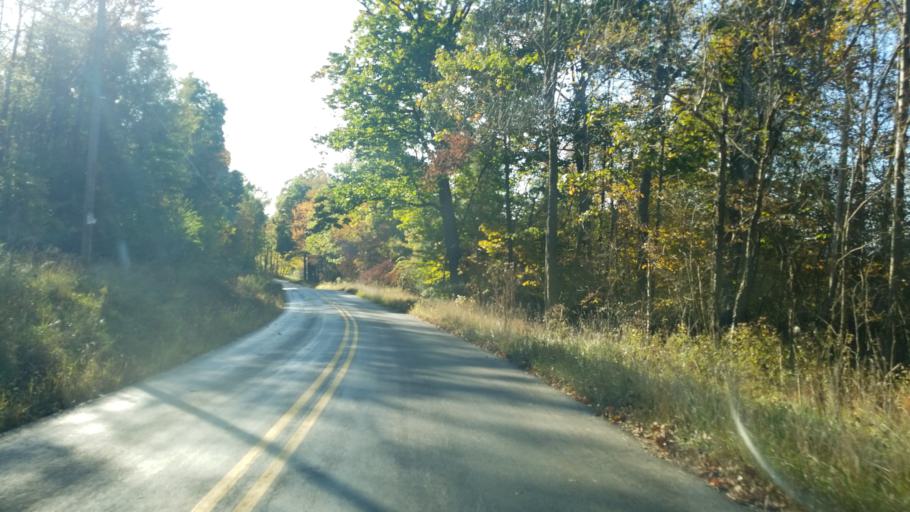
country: US
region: Pennsylvania
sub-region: Indiana County
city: Johnsonburg
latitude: 40.8970
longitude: -78.8894
